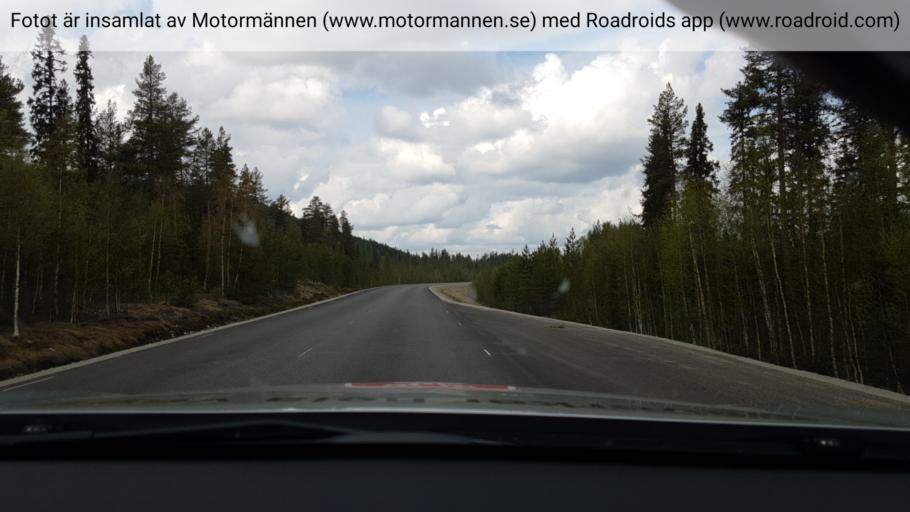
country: SE
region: Vaesterbotten
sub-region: Lycksele Kommun
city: Lycksele
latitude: 64.0264
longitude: 18.4456
